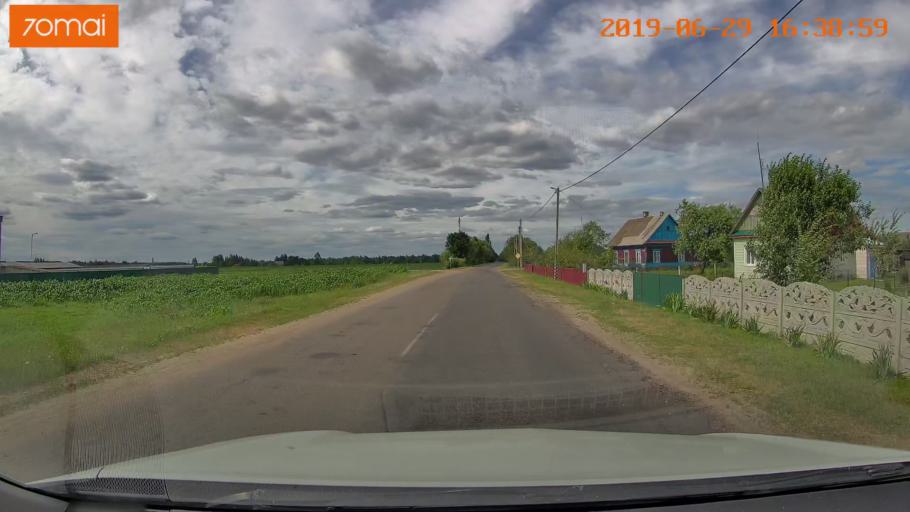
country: BY
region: Brest
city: Luninyets
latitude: 52.2375
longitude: 27.0155
